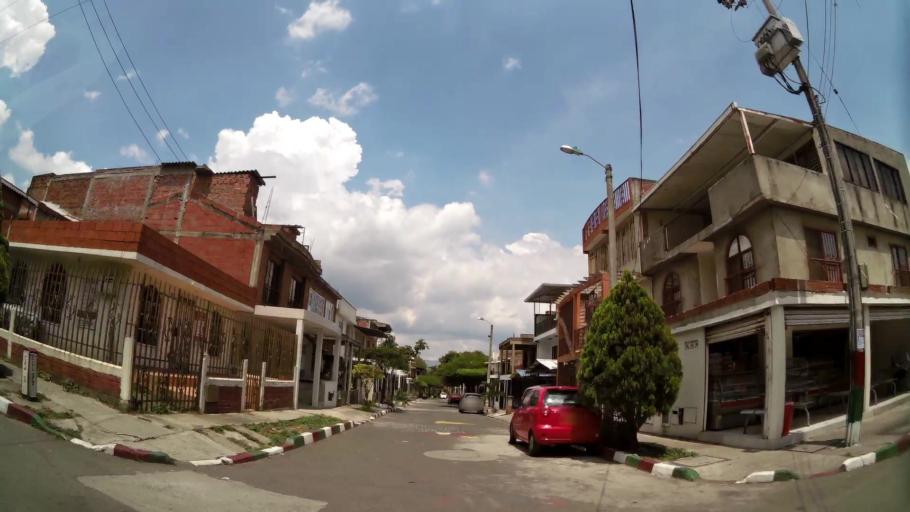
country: CO
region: Valle del Cauca
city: Cali
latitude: 3.4699
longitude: -76.4825
